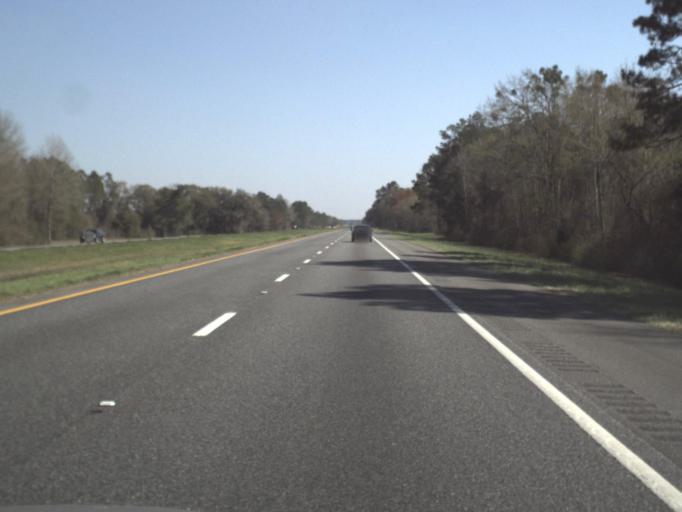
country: US
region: Florida
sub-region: Jackson County
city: Marianna
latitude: 30.7063
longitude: -85.1460
